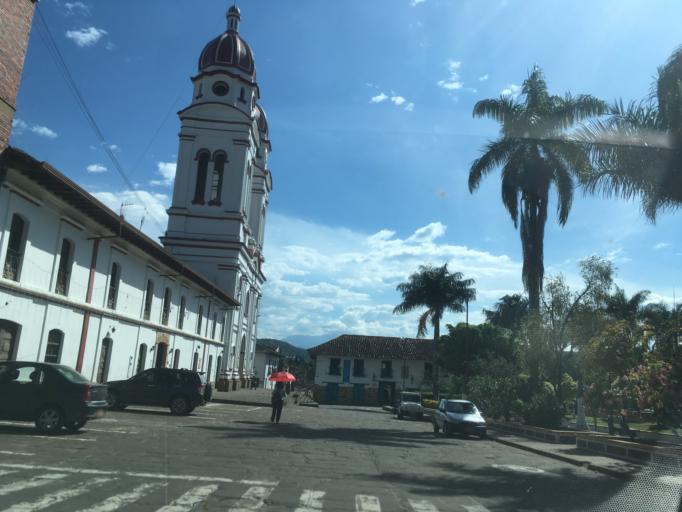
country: CO
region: Santander
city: Coromoro
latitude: 6.2884
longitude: -73.1480
